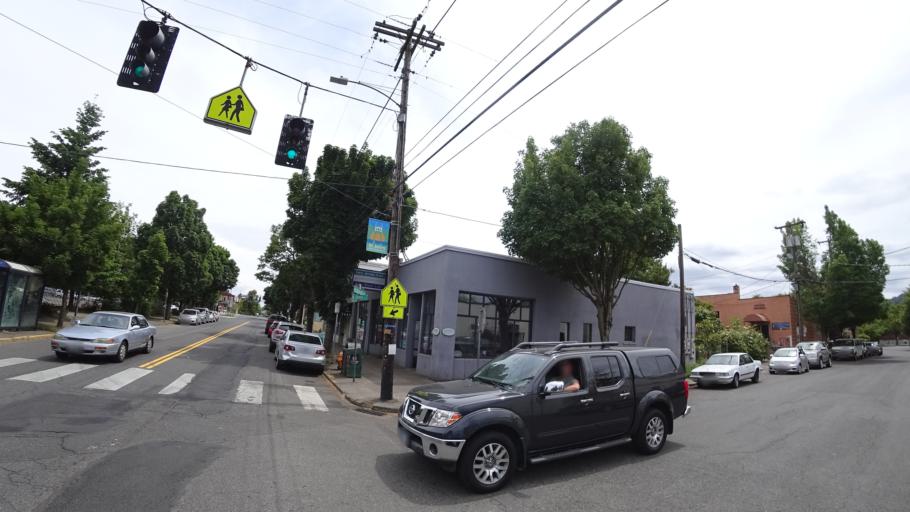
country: US
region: Oregon
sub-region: Washington County
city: West Haven
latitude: 45.5896
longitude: -122.7530
